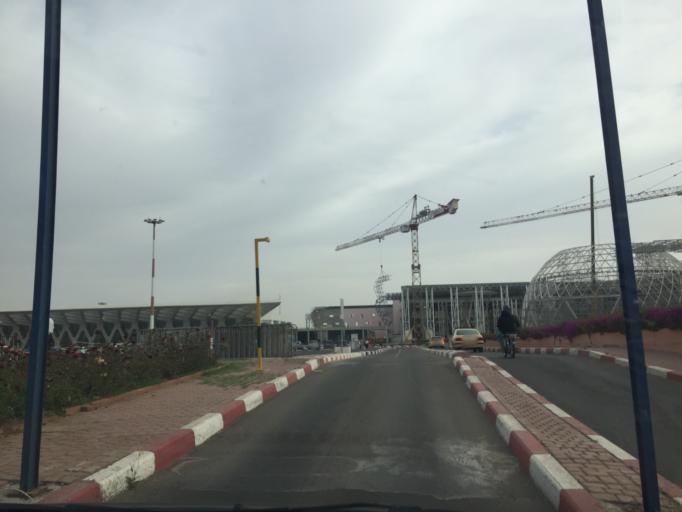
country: MA
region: Marrakech-Tensift-Al Haouz
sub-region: Marrakech
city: Marrakesh
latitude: 31.5994
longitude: -8.0258
